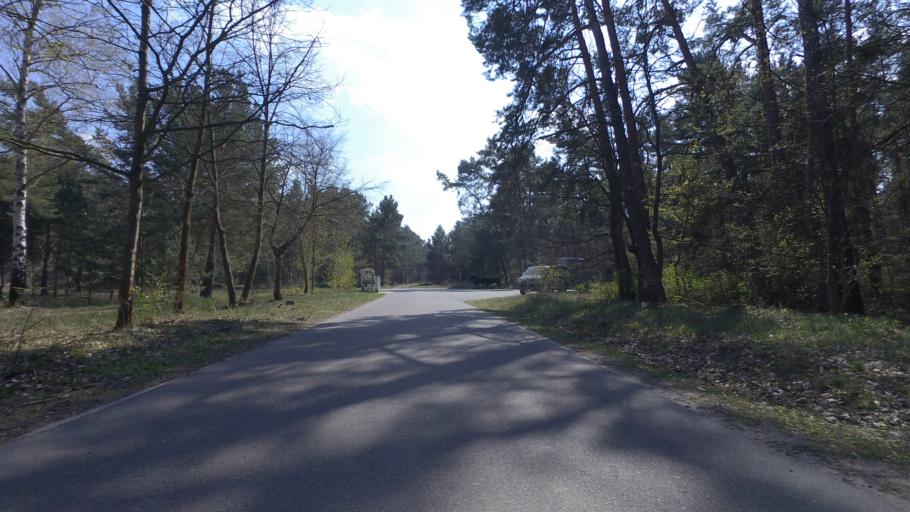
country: DE
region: Brandenburg
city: Mittenwalde
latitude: 52.2192
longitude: 13.5149
